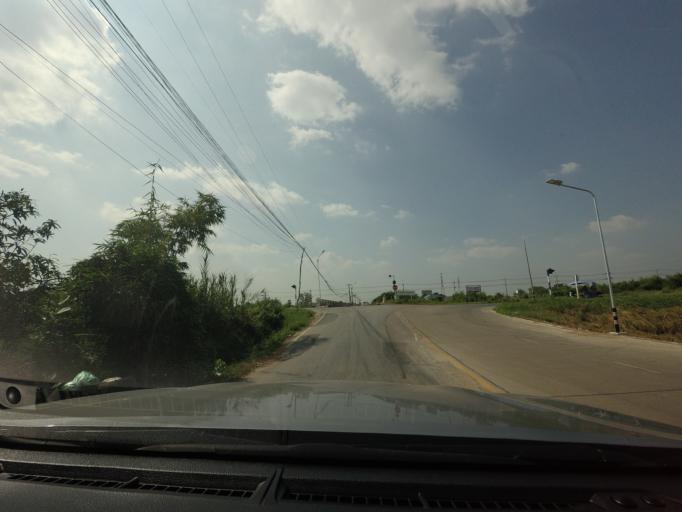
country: TH
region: Phitsanulok
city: Phitsanulok
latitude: 16.8226
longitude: 100.2361
